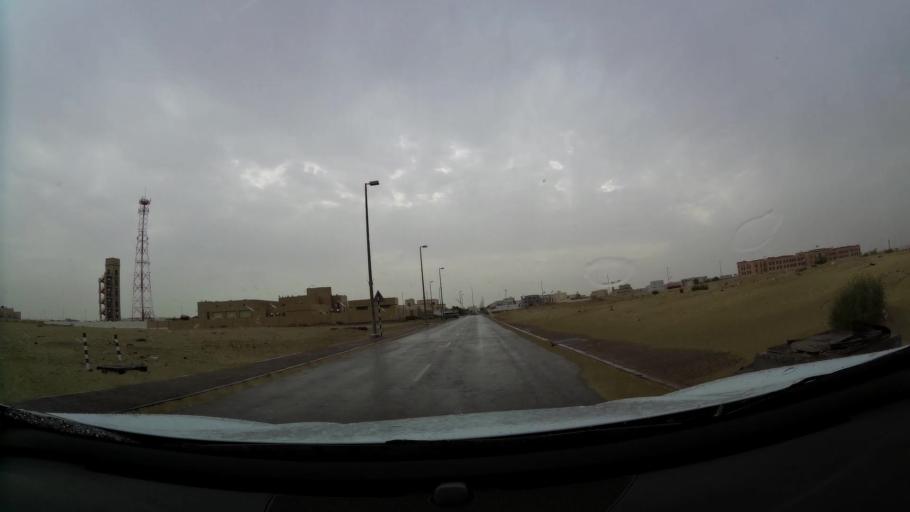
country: AE
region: Abu Dhabi
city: Abu Dhabi
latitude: 24.3618
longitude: 54.6376
